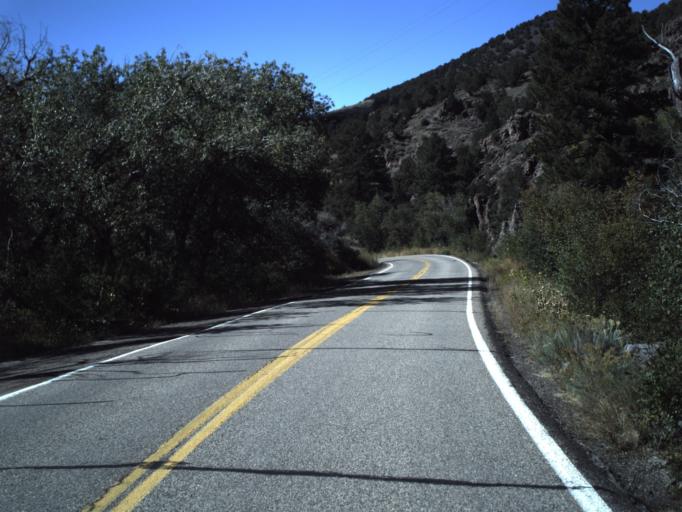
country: US
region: Utah
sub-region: Beaver County
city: Beaver
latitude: 38.2784
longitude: -112.5632
